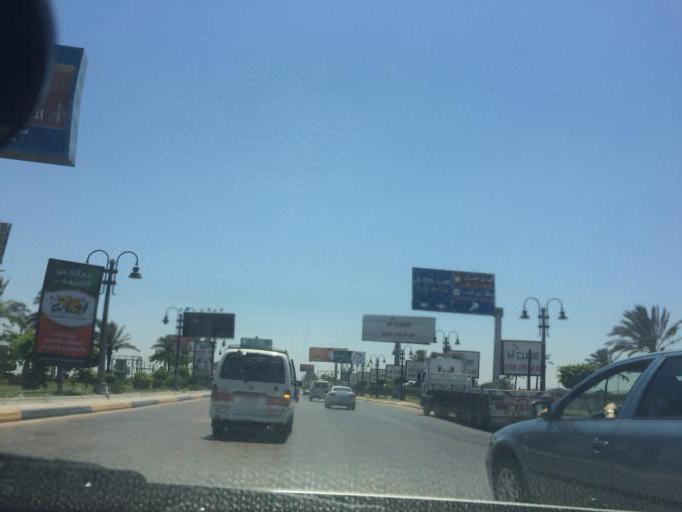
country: EG
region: Alexandria
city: Alexandria
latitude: 31.1659
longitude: 29.9350
